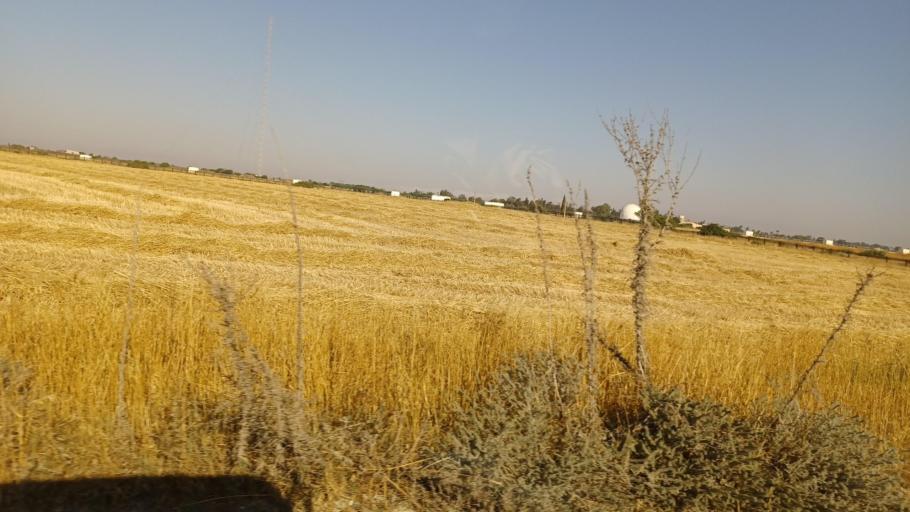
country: CY
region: Ammochostos
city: Frenaros
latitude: 35.0799
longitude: 33.9042
